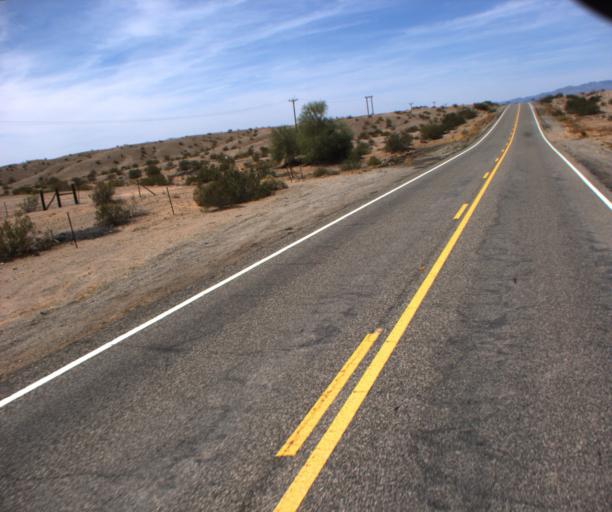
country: US
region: Arizona
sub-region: La Paz County
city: Parker
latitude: 34.0195
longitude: -114.2494
